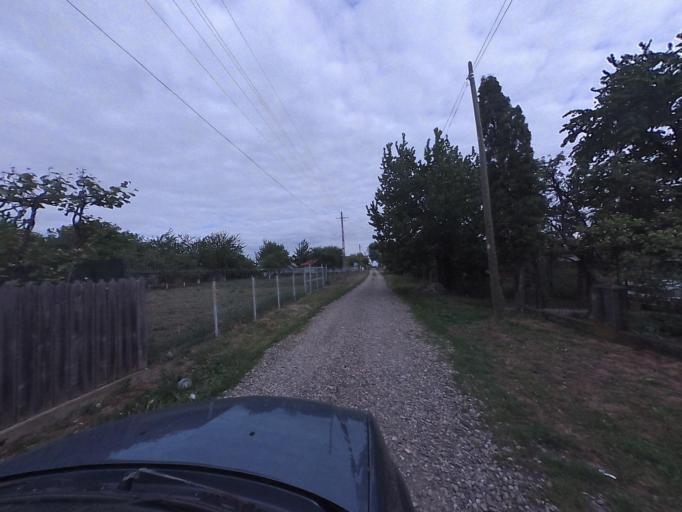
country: RO
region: Neamt
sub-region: Comuna Dulcesti
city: Dulcesti
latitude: 46.9594
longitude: 26.7975
